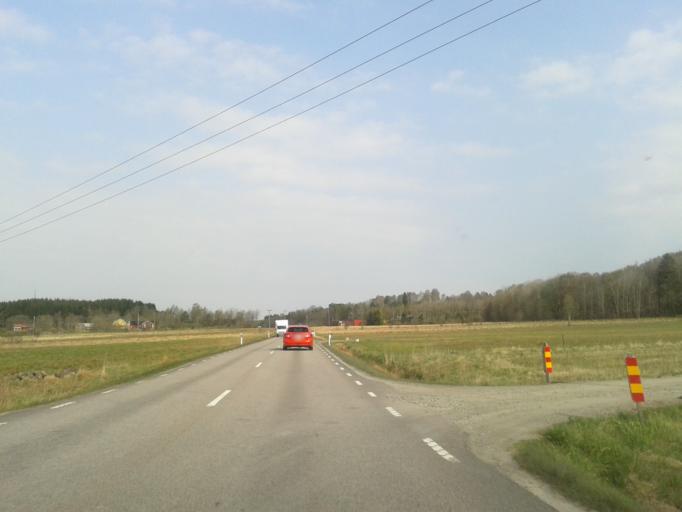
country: SE
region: Vaestra Goetaland
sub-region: Kungalvs Kommun
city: Kode
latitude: 57.8820
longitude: 11.8934
